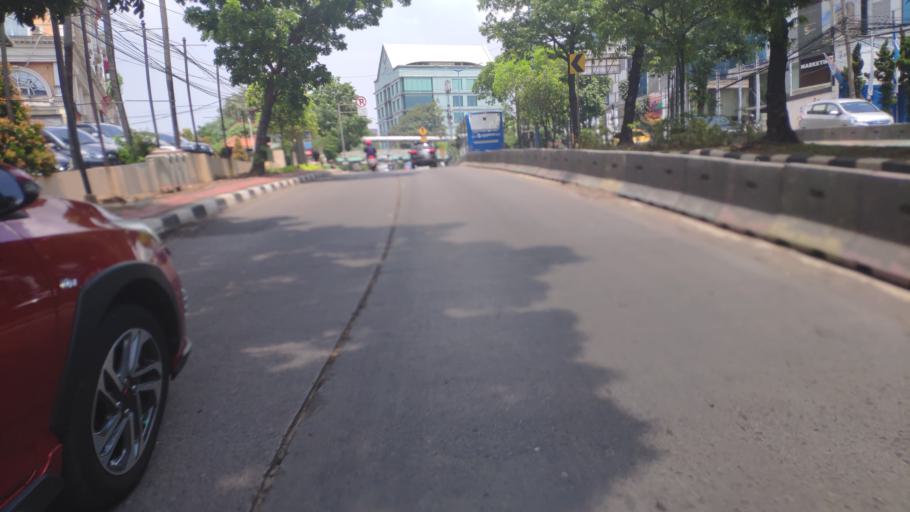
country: ID
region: Jakarta Raya
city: Jakarta
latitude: -6.2775
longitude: 106.8301
